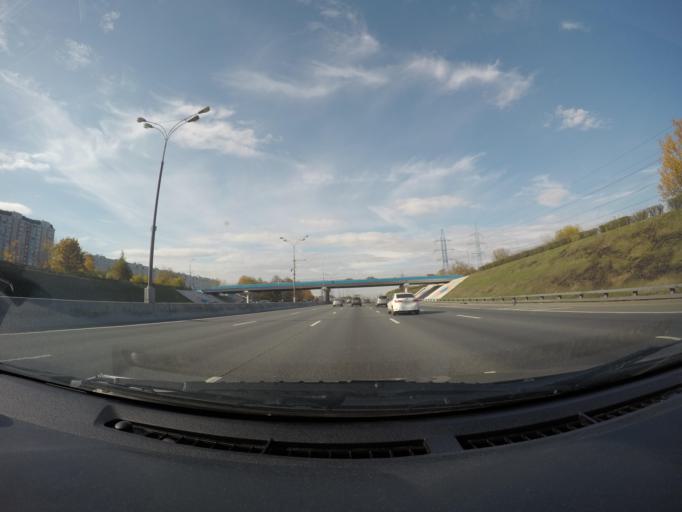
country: RU
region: Moscow
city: Bibirevo
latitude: 55.9023
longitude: 37.6166
